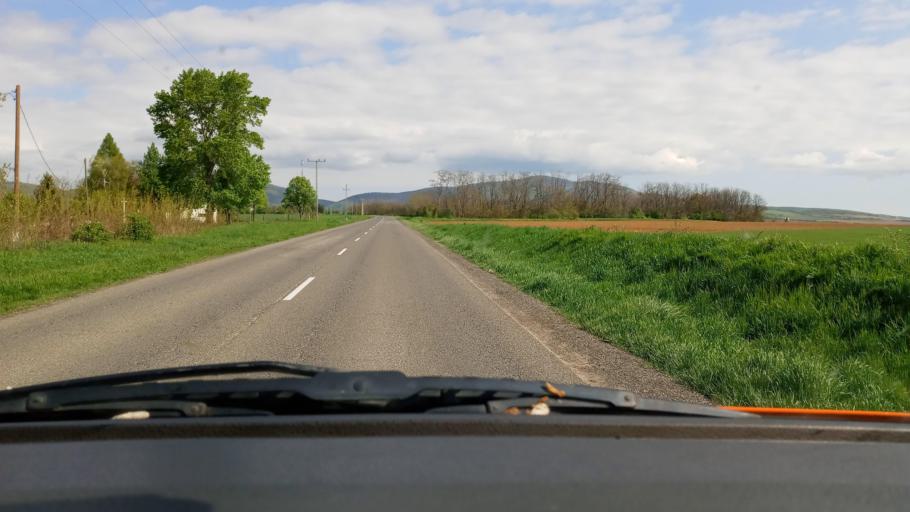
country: HU
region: Baranya
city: Hosszuheteny
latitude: 46.1189
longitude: 18.3481
